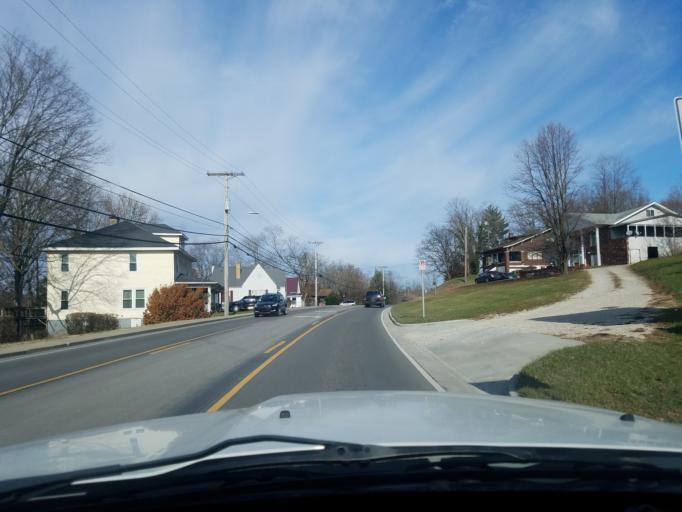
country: US
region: Indiana
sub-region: Orange County
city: Paoli
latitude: 38.5601
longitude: -86.4684
